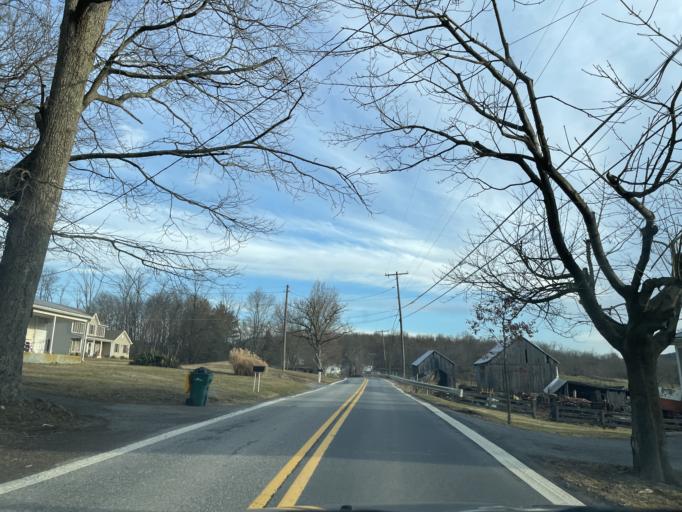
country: US
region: Maryland
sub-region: Washington County
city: Cavetown
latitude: 39.6081
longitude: -77.5563
